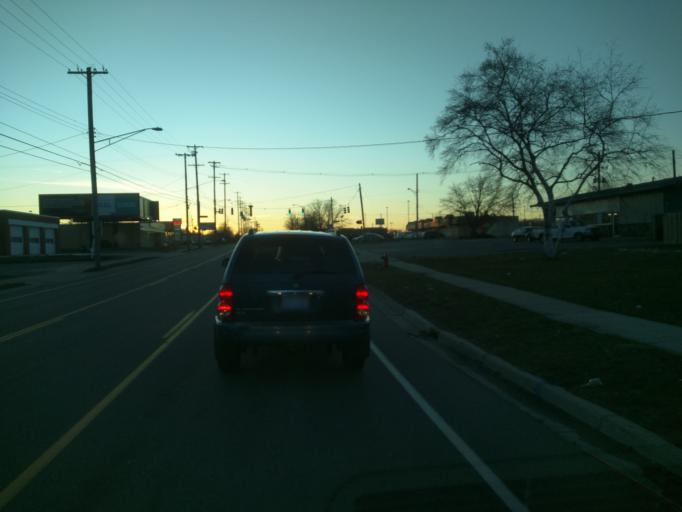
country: US
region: Michigan
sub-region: Ingham County
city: Lansing
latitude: 42.6975
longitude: -84.5631
